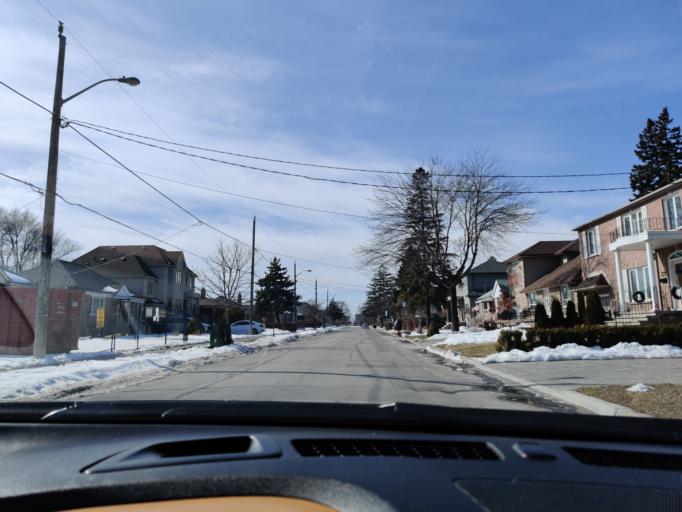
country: CA
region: Ontario
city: Toronto
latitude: 43.7163
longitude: -79.4398
